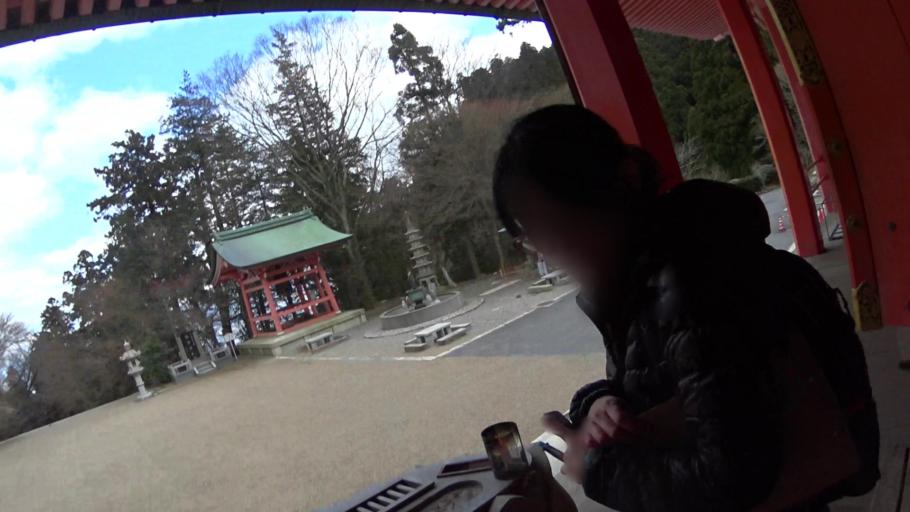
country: JP
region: Shiga Prefecture
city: Otsu-shi
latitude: 35.0687
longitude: 135.8383
